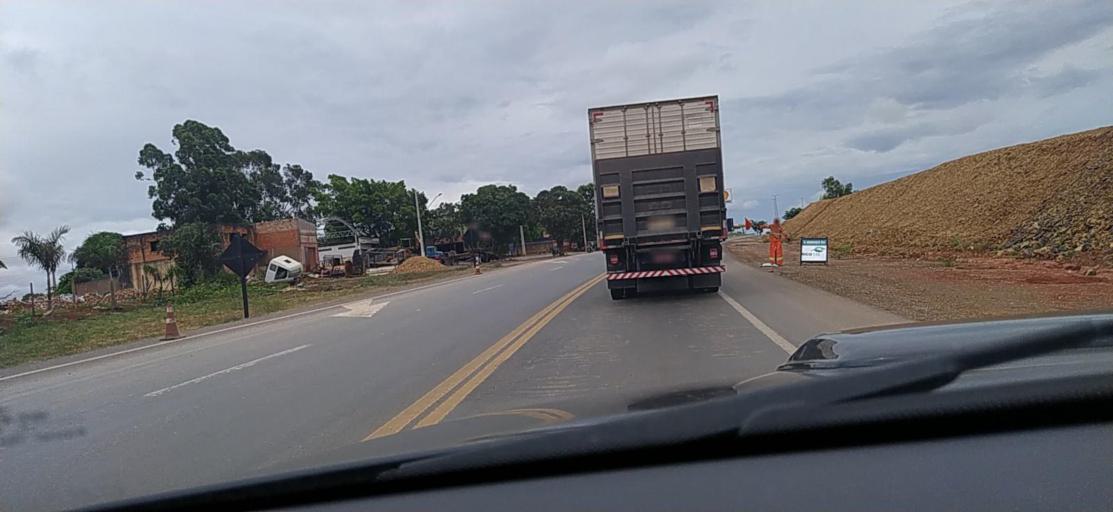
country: BR
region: Minas Gerais
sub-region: Curvelo
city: Curvelo
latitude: -18.7122
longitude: -44.4428
